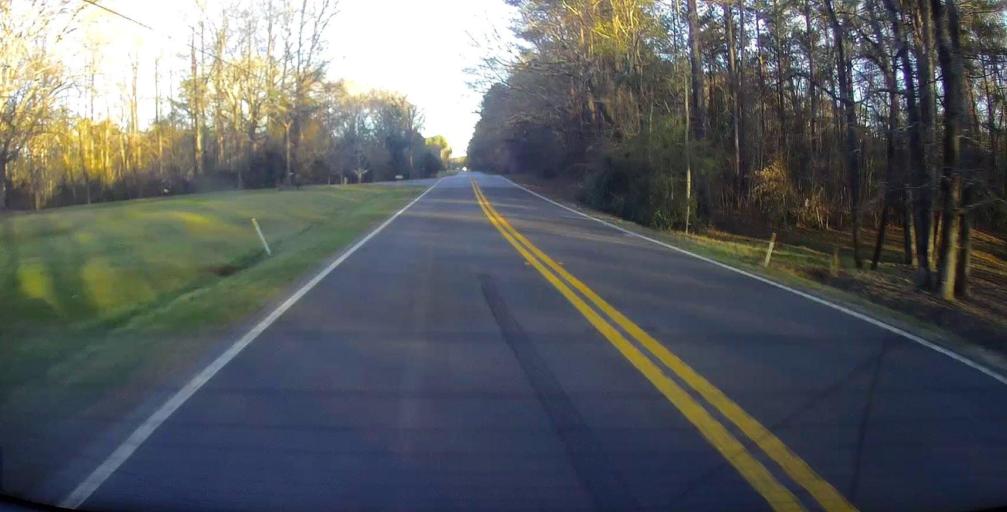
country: US
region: Georgia
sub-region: Harris County
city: Hamilton
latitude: 32.6680
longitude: -84.8772
